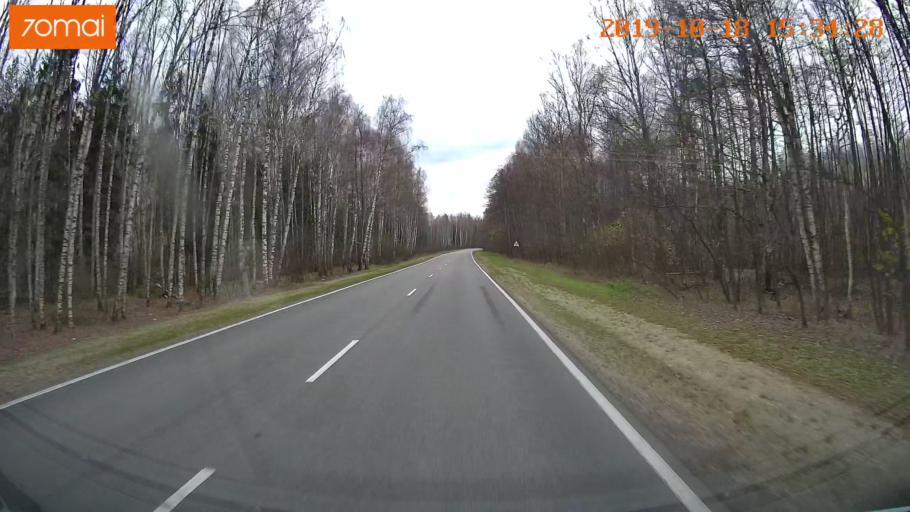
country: RU
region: Vladimir
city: Anopino
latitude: 55.8546
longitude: 40.6422
